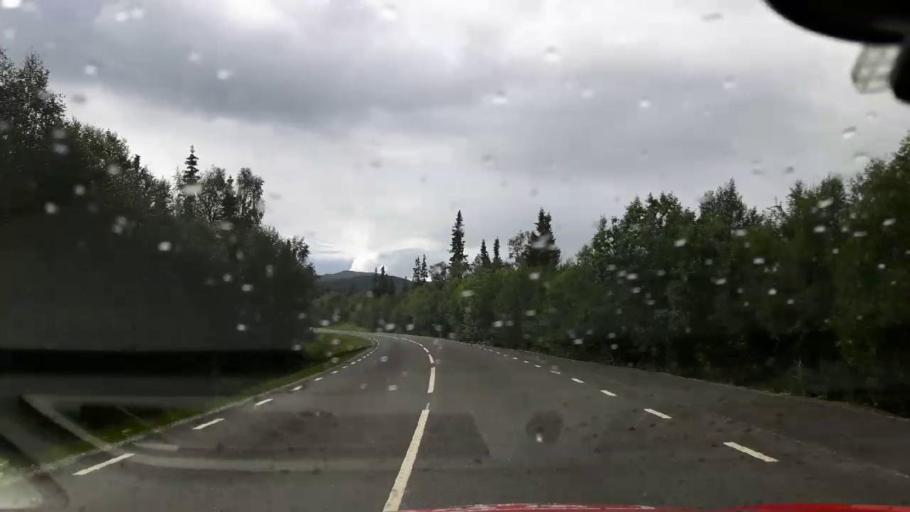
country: NO
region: Nord-Trondelag
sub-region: Royrvik
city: Royrvik
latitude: 64.9014
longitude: 14.1923
